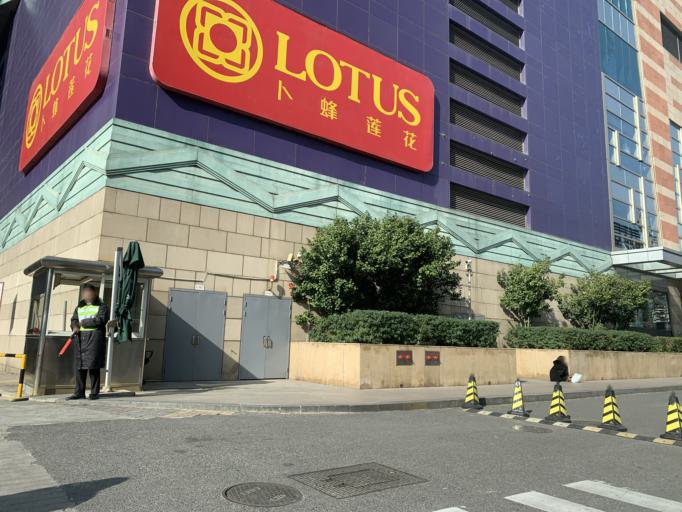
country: CN
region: Shanghai Shi
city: Hongkou
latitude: 31.2386
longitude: 121.4960
